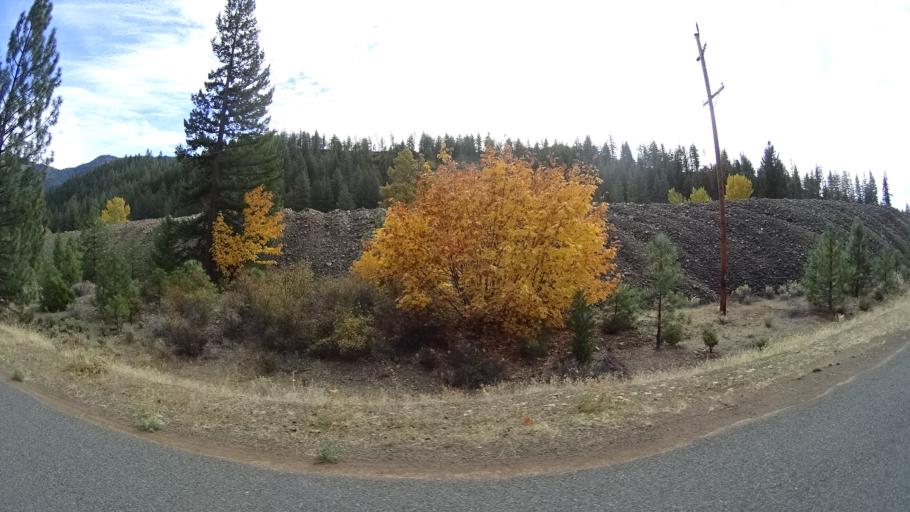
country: US
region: California
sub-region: Siskiyou County
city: Yreka
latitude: 41.6825
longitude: -122.8266
